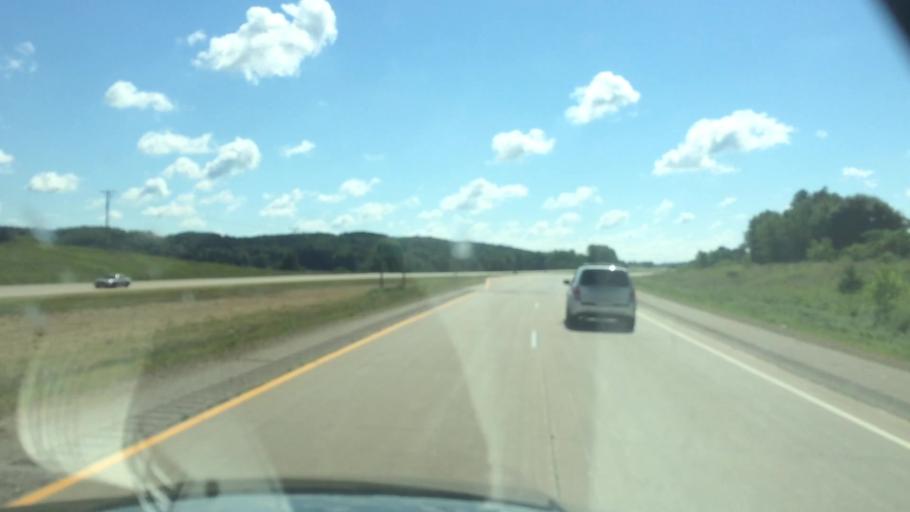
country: US
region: Wisconsin
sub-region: Portage County
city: Amherst
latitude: 44.5013
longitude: -89.3847
